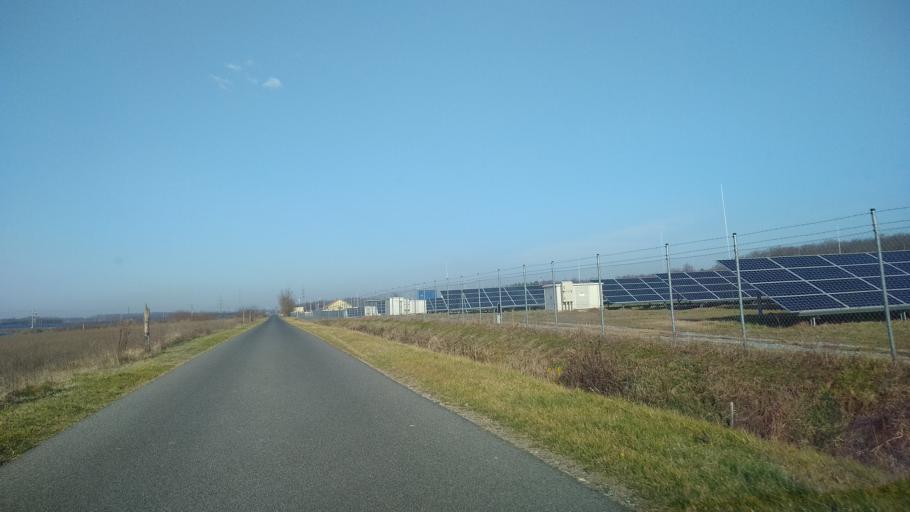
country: HU
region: Somogy
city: Barcs
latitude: 45.9680
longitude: 17.4977
